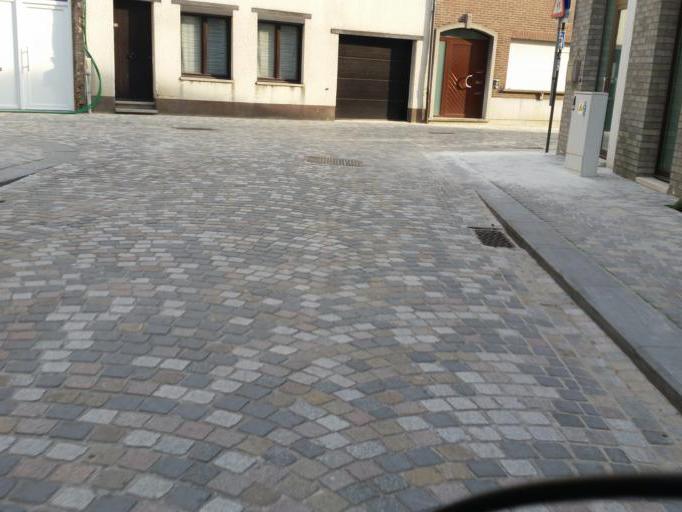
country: BE
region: Flanders
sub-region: Provincie Antwerpen
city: Mechelen
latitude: 51.0265
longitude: 4.4840
